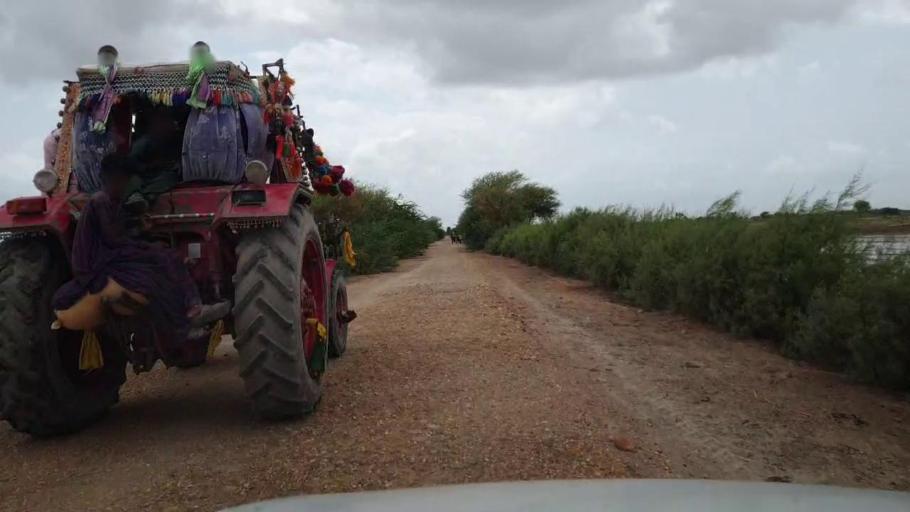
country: PK
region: Sindh
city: Kario
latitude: 24.7491
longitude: 68.4764
